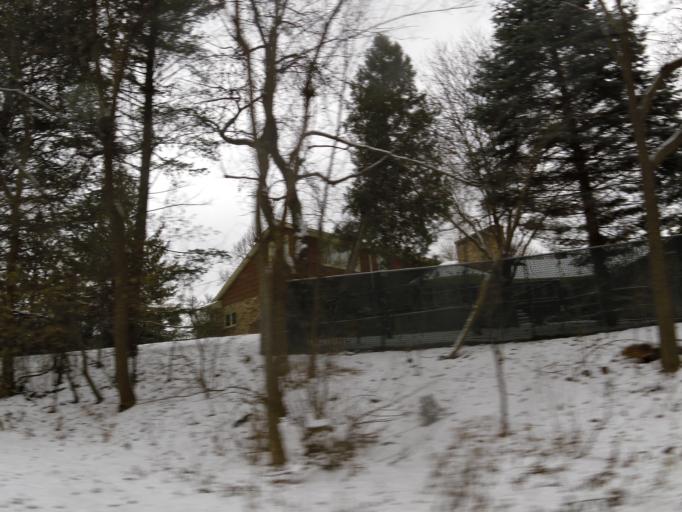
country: US
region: Minnesota
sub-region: Dakota County
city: Mendota Heights
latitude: 44.9067
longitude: -93.1661
